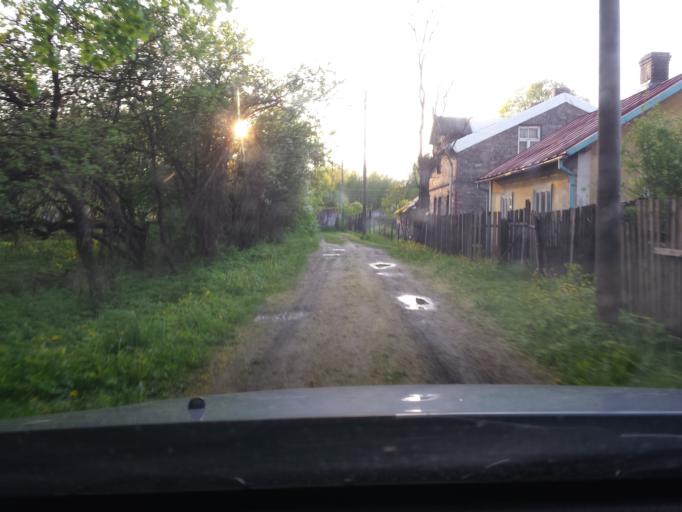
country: LV
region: Riga
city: Bolderaja
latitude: 57.0011
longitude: 24.1010
